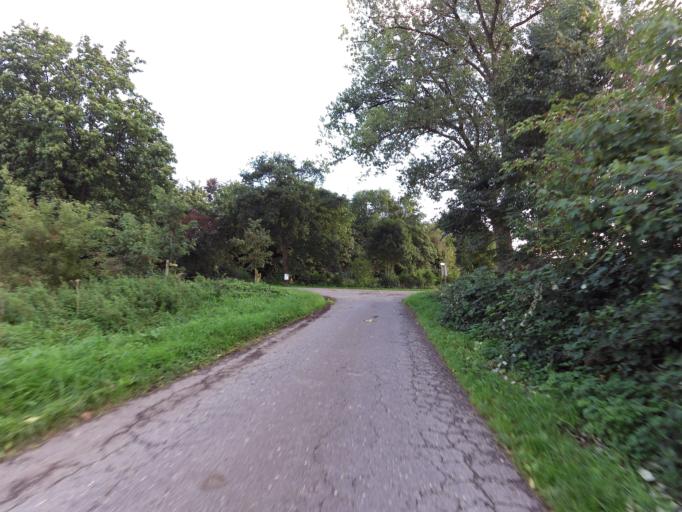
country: NL
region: Gelderland
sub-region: Gemeente Montferland
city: s-Heerenberg
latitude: 51.8624
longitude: 6.2717
